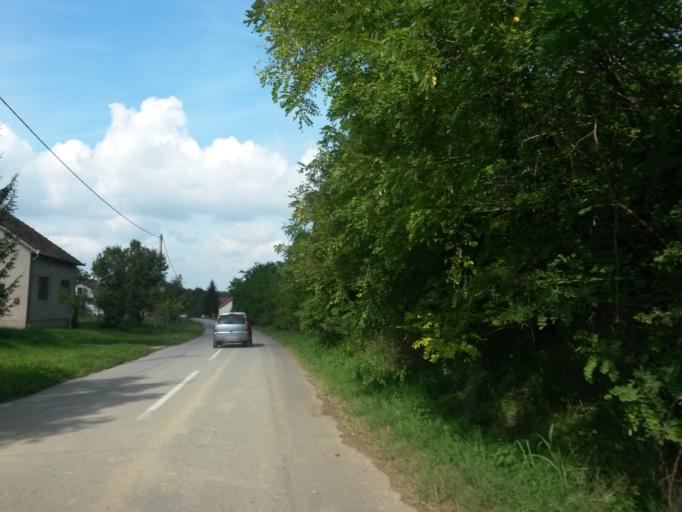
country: HR
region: Vukovarsko-Srijemska
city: Ilok
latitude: 45.2136
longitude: 19.3858
